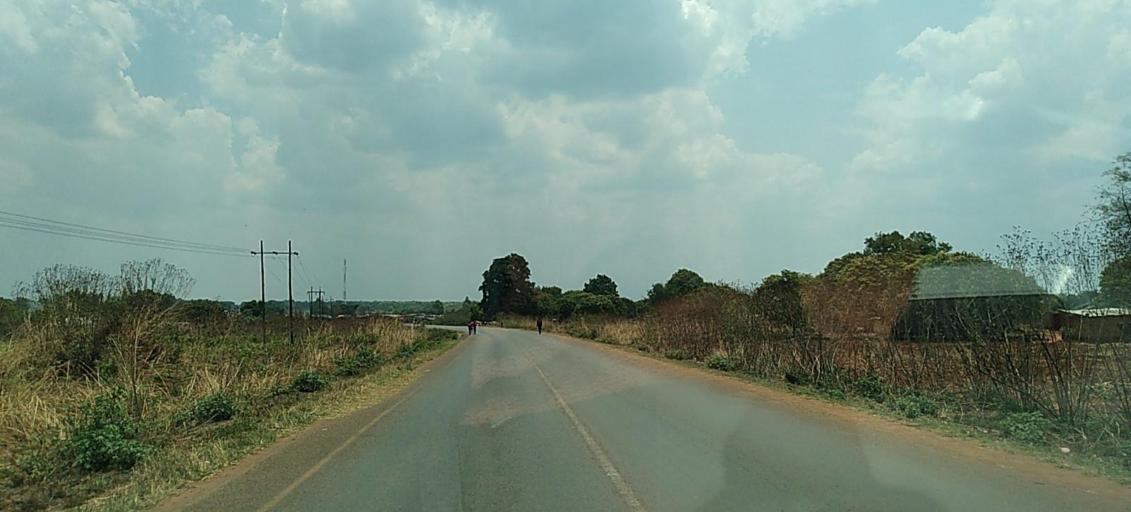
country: ZM
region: Copperbelt
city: Kalulushi
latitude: -12.8345
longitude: 27.9726
